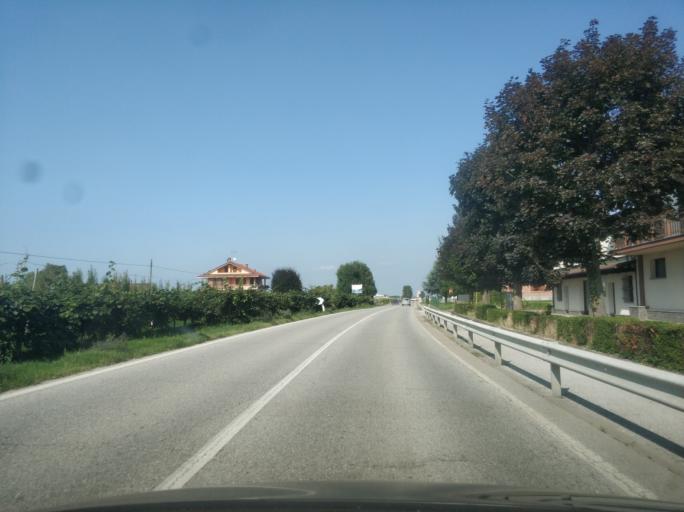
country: IT
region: Piedmont
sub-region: Provincia di Cuneo
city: Centallo
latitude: 44.5099
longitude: 7.5906
